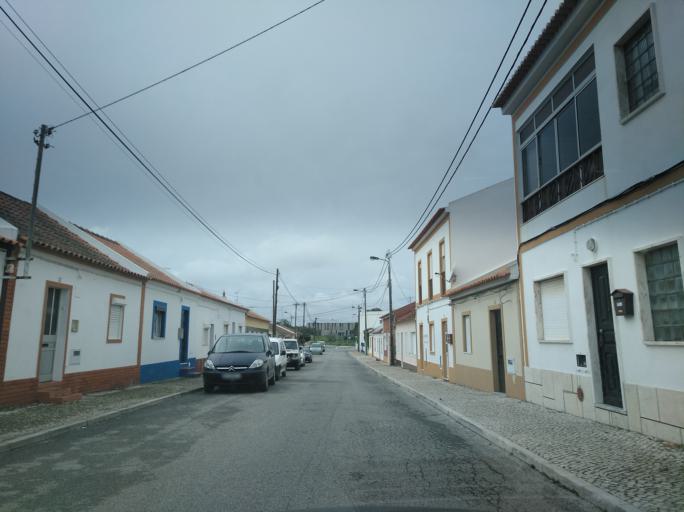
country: PT
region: Setubal
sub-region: Grandola
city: Grandola
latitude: 38.1792
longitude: -8.5710
